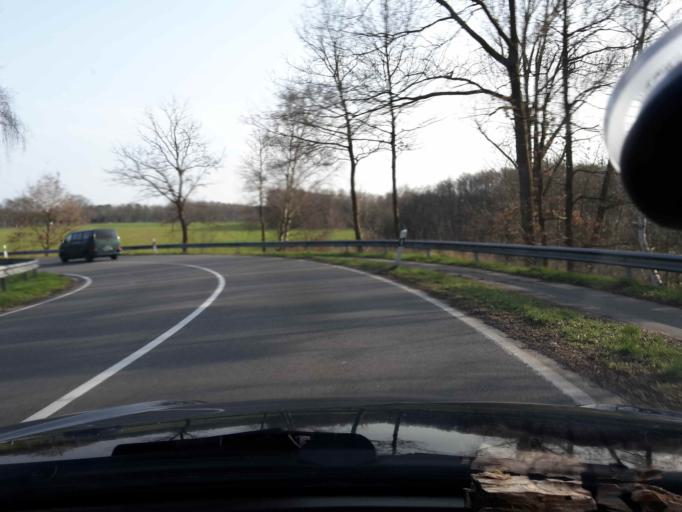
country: DE
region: Lower Saxony
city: Buxtehude
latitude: 53.4608
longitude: 9.6940
